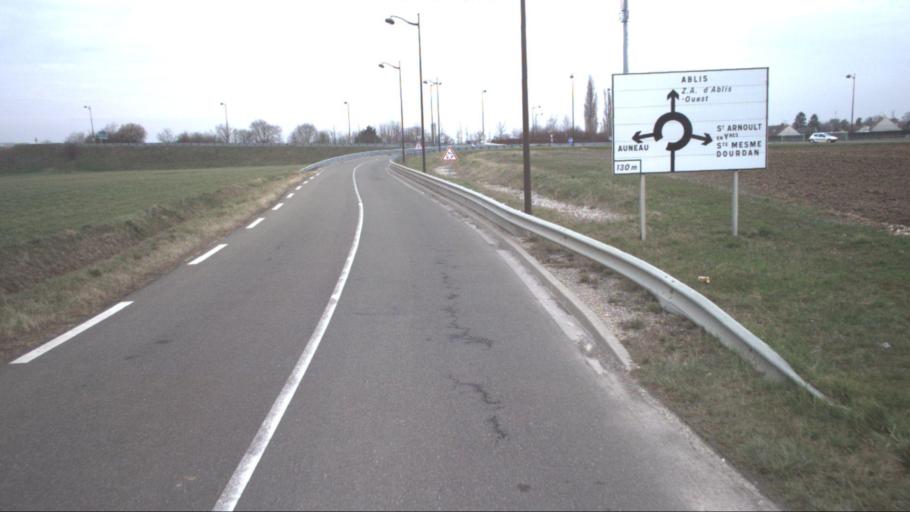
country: FR
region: Ile-de-France
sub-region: Departement des Yvelines
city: Ablis
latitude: 48.5086
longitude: 1.8350
